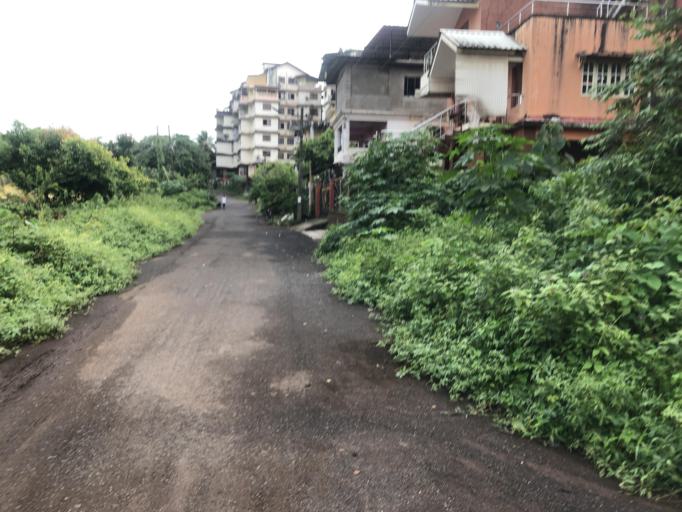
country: IN
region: Goa
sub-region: North Goa
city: Serula
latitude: 15.5469
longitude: 73.8258
